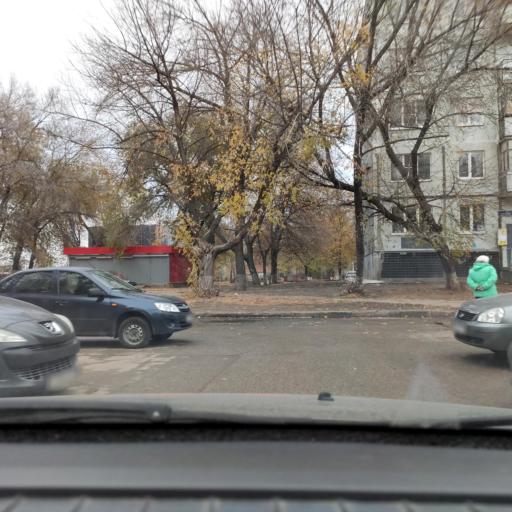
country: RU
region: Samara
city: Tol'yatti
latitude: 53.5251
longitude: 49.2987
